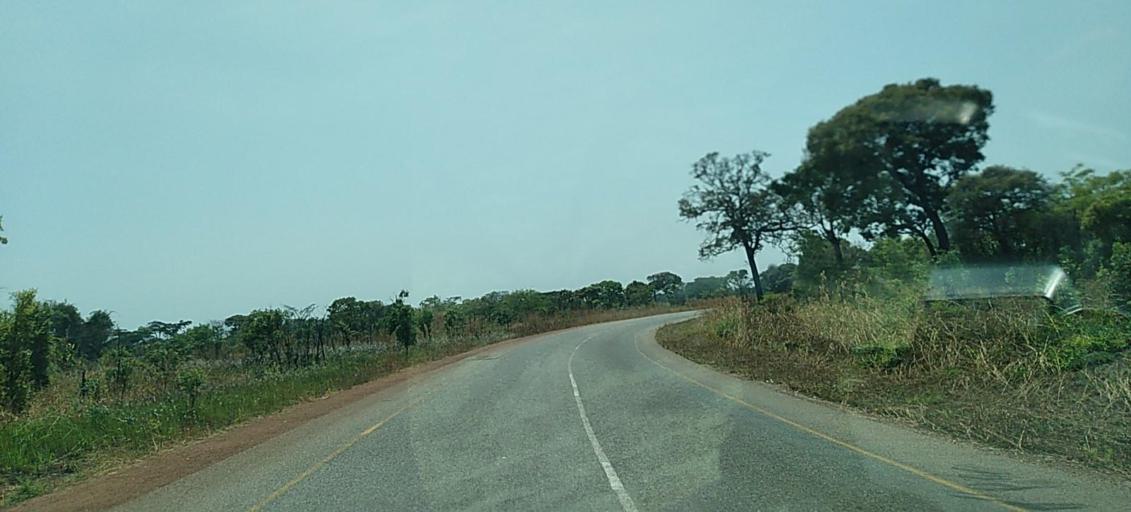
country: ZM
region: North-Western
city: Solwezi
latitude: -12.3796
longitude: 26.1879
